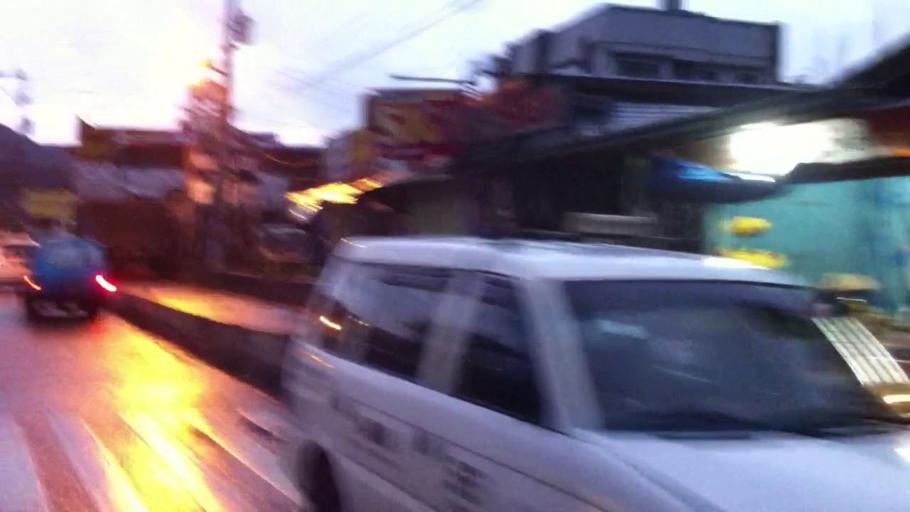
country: PH
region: Cordillera
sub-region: Province of Benguet
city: La Trinidad
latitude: 16.4453
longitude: 120.5861
